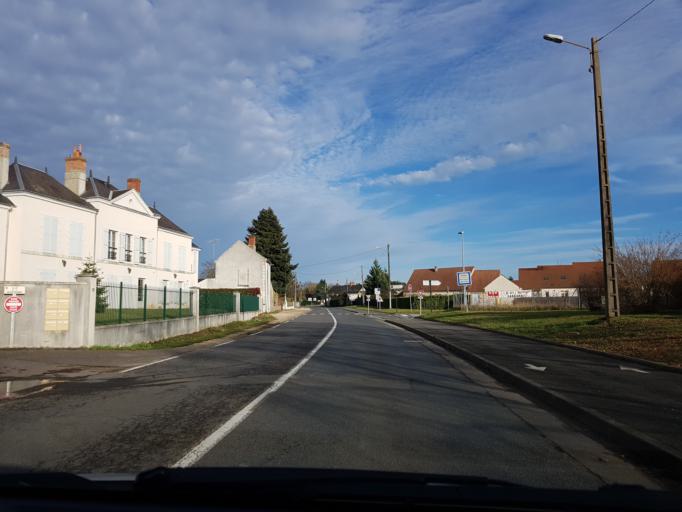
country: FR
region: Centre
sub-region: Departement du Loiret
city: Darvoy
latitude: 47.8621
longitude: 2.1115
